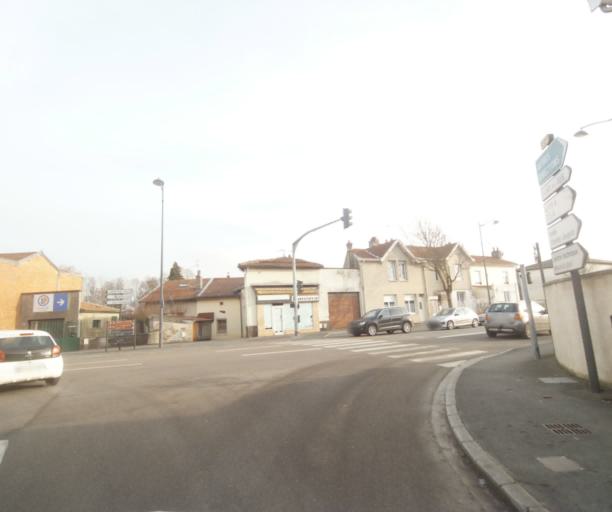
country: FR
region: Champagne-Ardenne
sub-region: Departement de la Haute-Marne
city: Saint-Dizier
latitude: 48.6295
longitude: 4.9554
